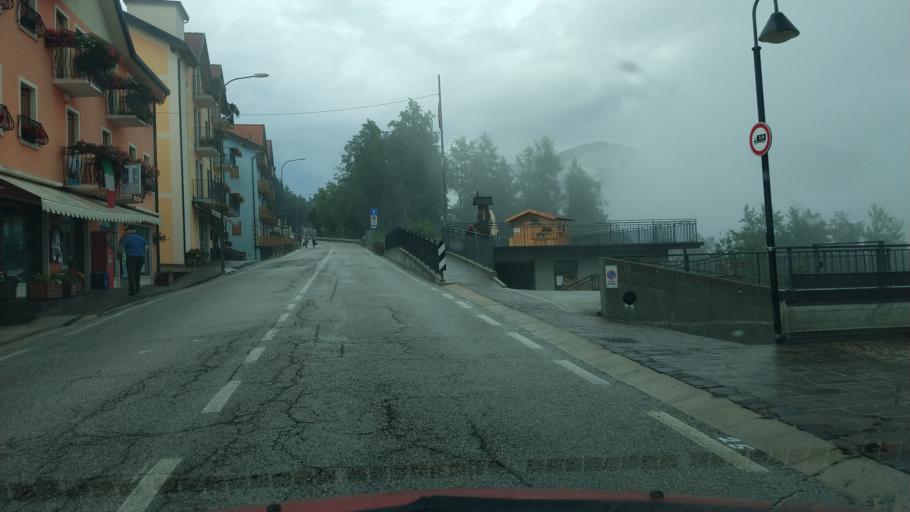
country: IT
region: Veneto
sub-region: Provincia di Vicenza
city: Tonezza del Cimone
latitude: 45.8595
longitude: 11.3472
